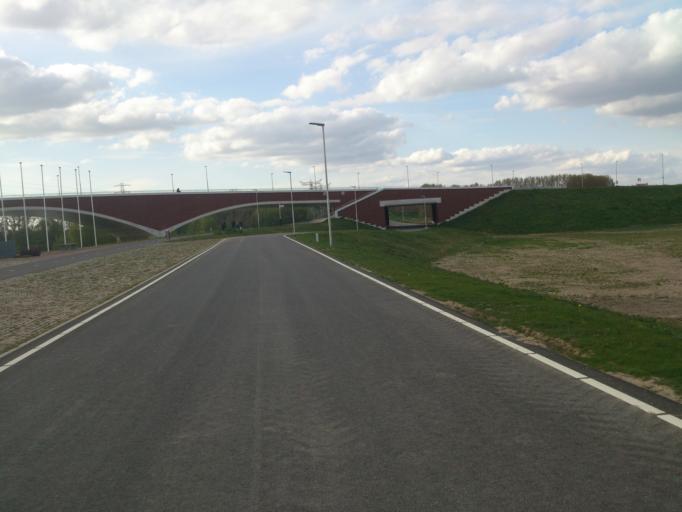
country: NL
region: Gelderland
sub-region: Gemeente Nijmegen
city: Nijmegen
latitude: 51.8634
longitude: 5.8477
